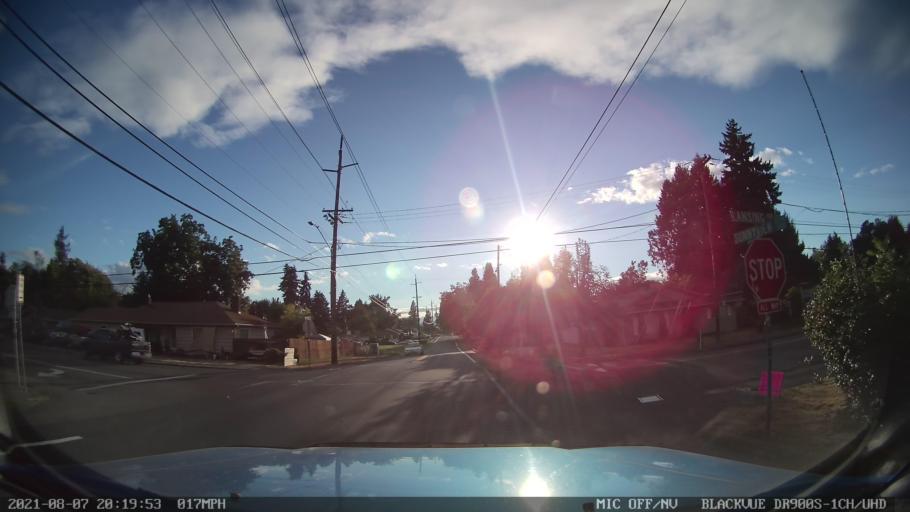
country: US
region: Oregon
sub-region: Marion County
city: Four Corners
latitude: 44.9540
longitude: -122.9975
